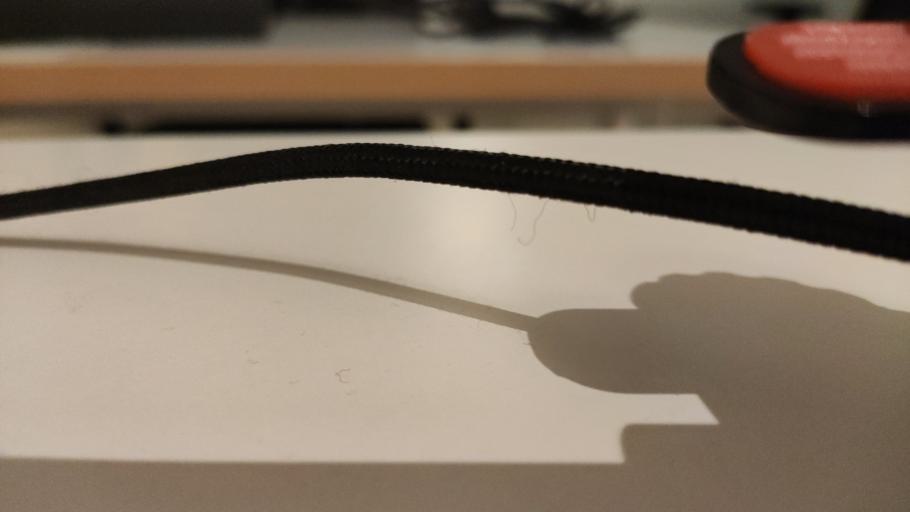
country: RU
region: Moskovskaya
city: Semkhoz
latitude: 56.4019
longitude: 38.0269
